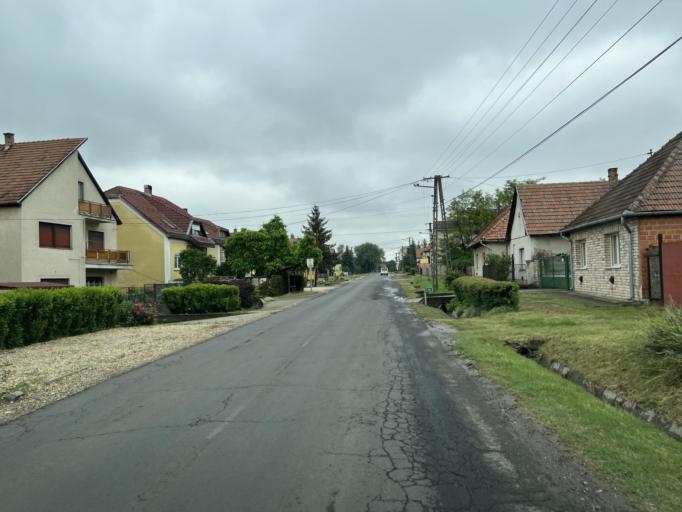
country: HU
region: Pest
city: Galgaheviz
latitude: 47.6188
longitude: 19.5691
